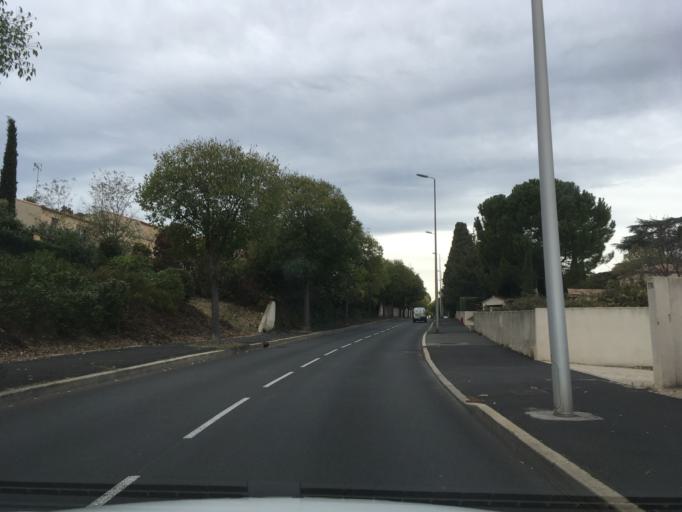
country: FR
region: Languedoc-Roussillon
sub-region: Departement de l'Herault
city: Castelnau-le-Lez
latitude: 43.6318
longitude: 3.8833
